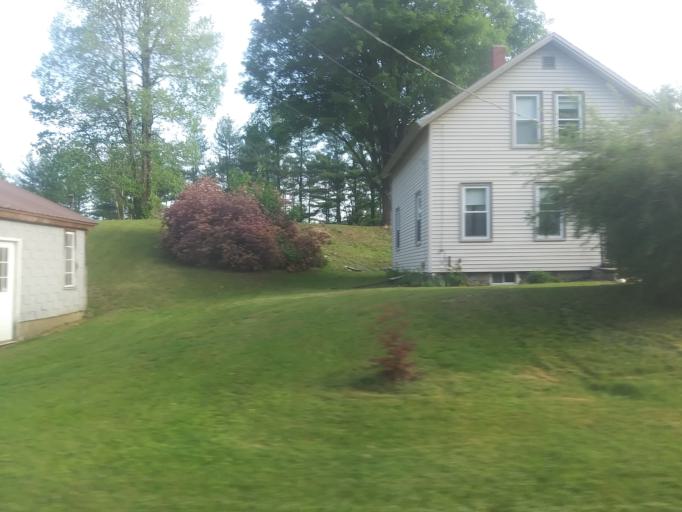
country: US
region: Massachusetts
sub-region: Franklin County
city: Shelburne Falls
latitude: 42.6127
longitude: -72.7643
